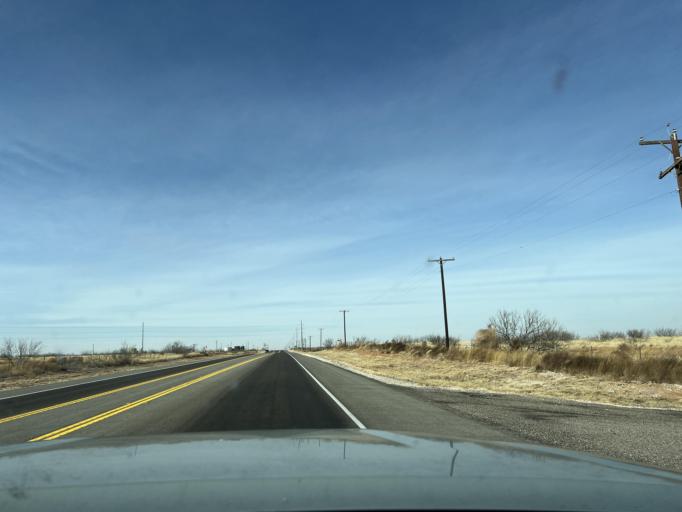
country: US
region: Texas
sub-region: Andrews County
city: Andrews
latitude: 32.3326
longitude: -102.6521
